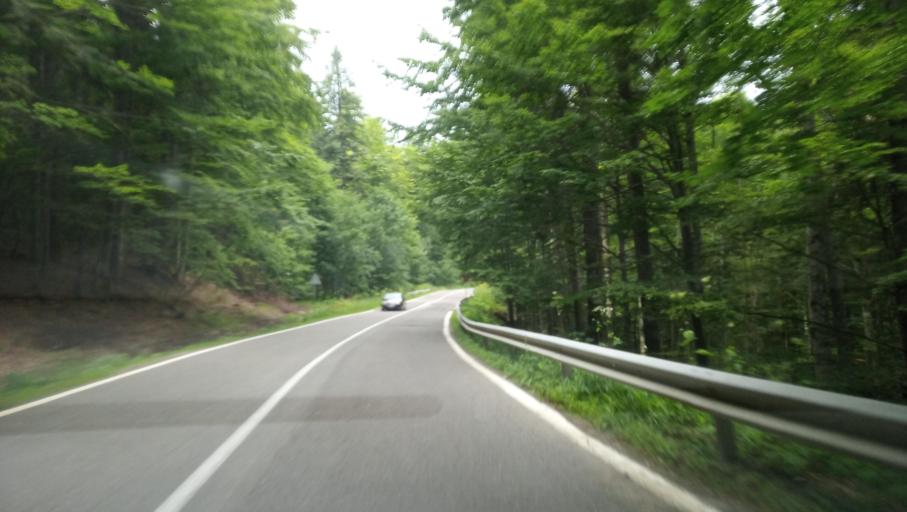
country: RO
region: Prahova
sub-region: Oras Sinaia
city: Sinaia
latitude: 45.3161
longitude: 25.5209
